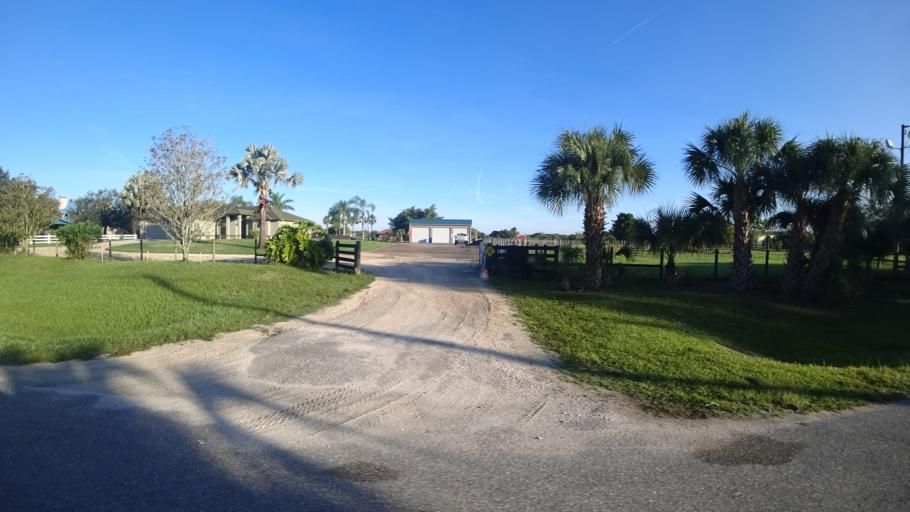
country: US
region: Florida
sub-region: Manatee County
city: Ellenton
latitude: 27.5398
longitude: -82.5220
